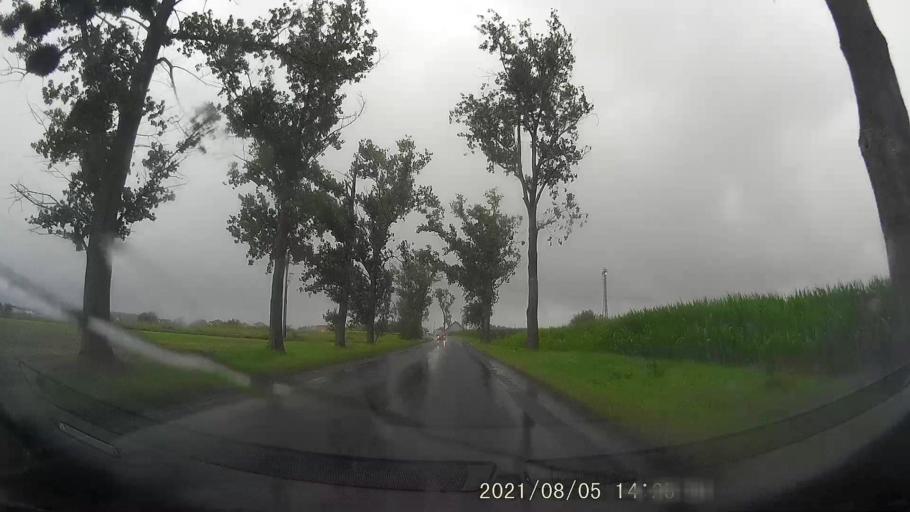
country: PL
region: Opole Voivodeship
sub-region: Powiat nyski
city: Korfantow
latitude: 50.4850
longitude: 17.6096
